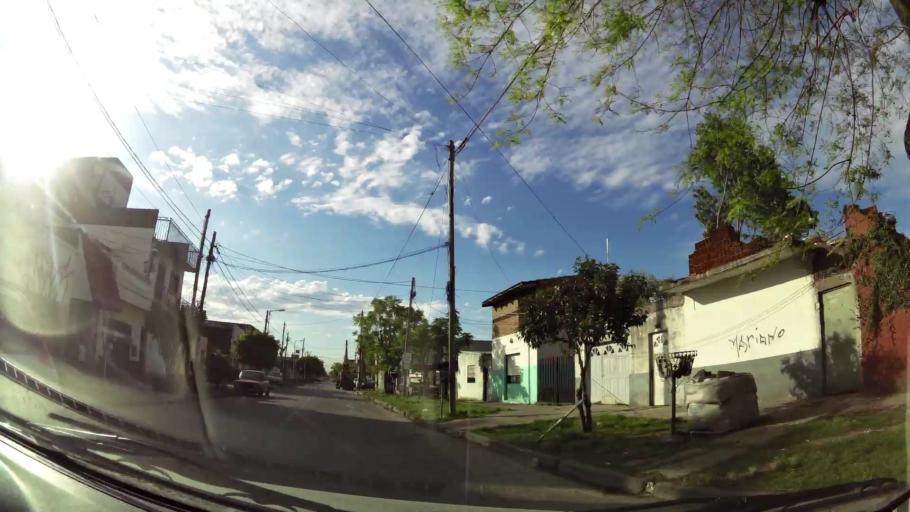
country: AR
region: Buenos Aires
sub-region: Partido de Lanus
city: Lanus
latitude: -34.7087
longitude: -58.3472
